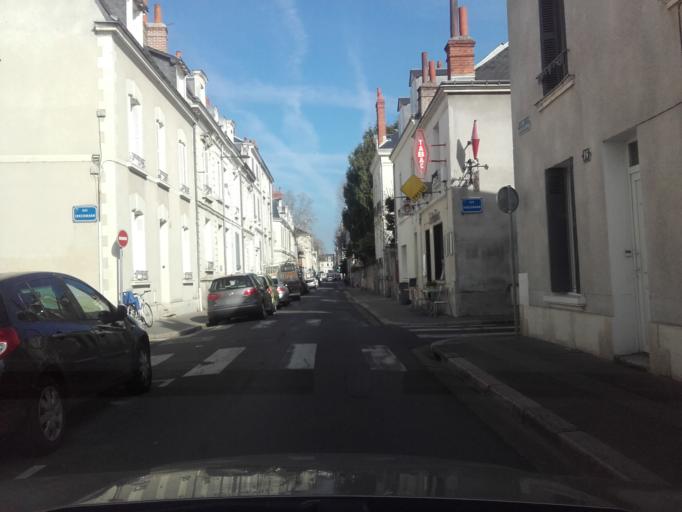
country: FR
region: Centre
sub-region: Departement d'Indre-et-Loire
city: Tours
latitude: 47.3878
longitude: 0.6848
